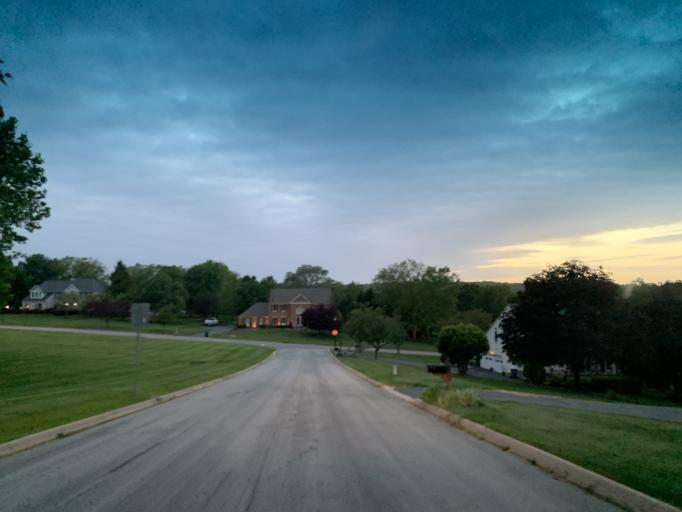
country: US
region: Maryland
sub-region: Harford County
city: South Bel Air
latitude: 39.5939
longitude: -76.2671
